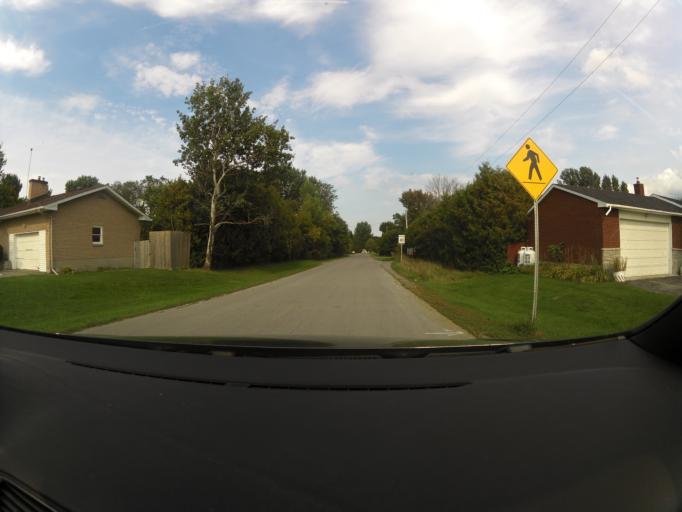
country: CA
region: Ontario
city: Carleton Place
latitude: 45.3584
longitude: -76.1225
